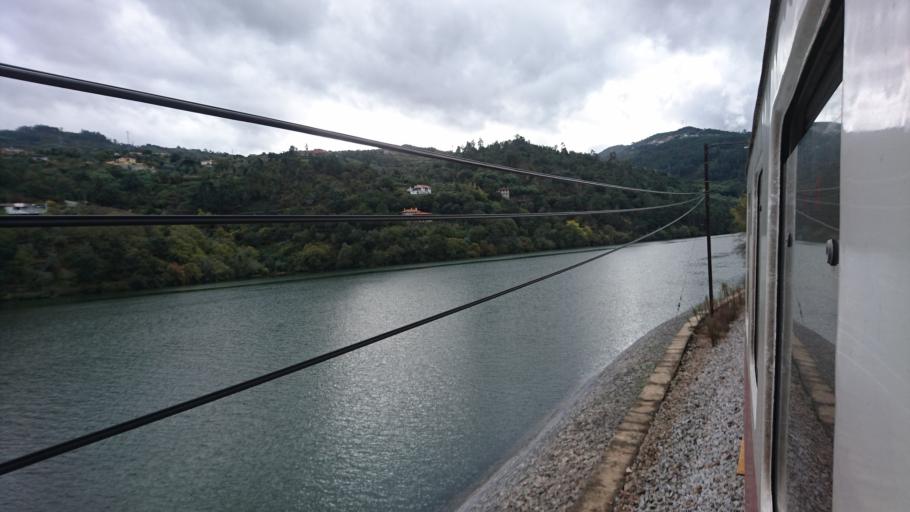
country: PT
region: Viseu
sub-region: Resende
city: Resende
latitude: 41.1025
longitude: -8.0193
